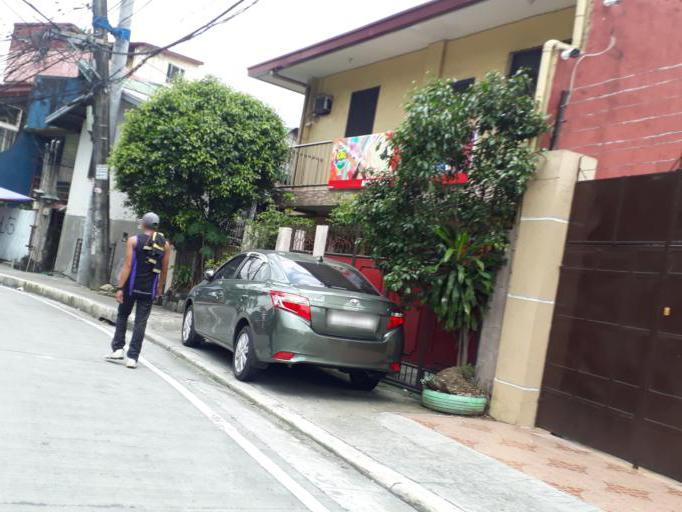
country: PH
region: Calabarzon
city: Bagong Pagasa
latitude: 14.6619
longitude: 121.0281
